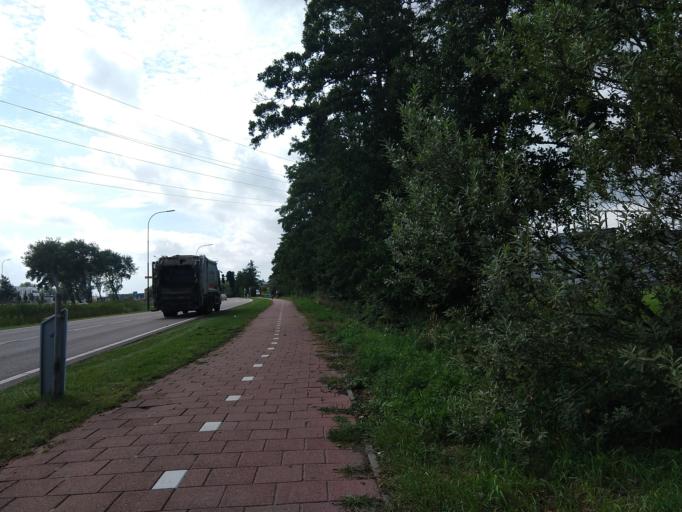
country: NL
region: Zeeland
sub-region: Gemeente Vlissingen
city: Vlissingen
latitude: 51.4530
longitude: 3.5924
